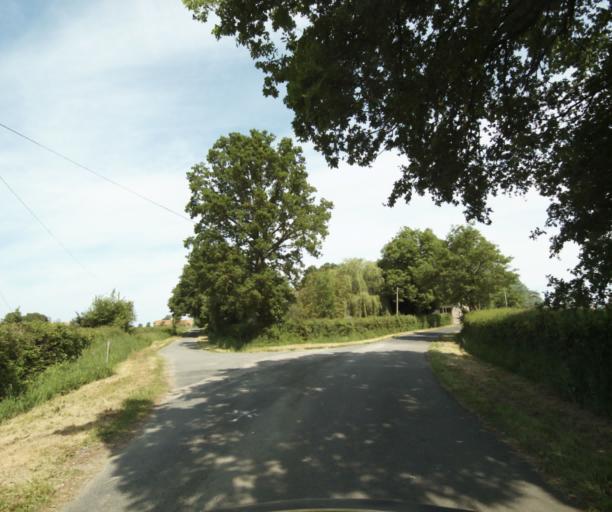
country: FR
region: Bourgogne
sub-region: Departement de Saone-et-Loire
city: Palinges
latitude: 46.5606
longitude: 4.1773
